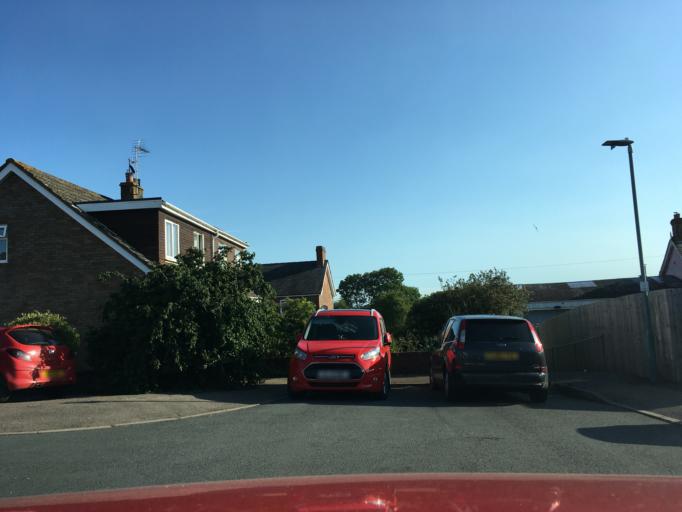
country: GB
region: Wales
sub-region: Monmouthshire
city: Tintern
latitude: 51.7371
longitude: -2.6381
